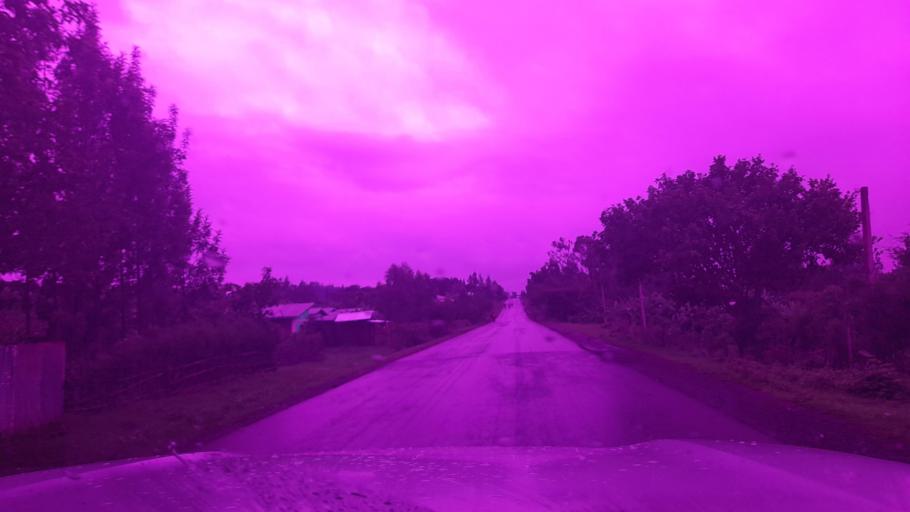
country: ET
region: Oromiya
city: Jima
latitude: 7.8118
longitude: 37.3435
